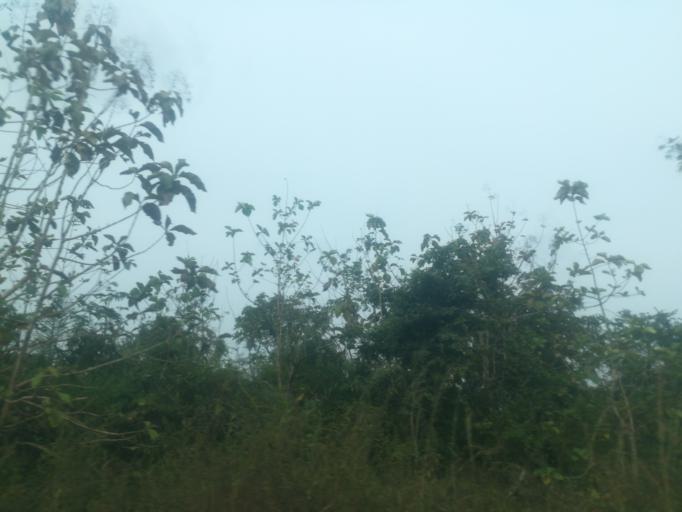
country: NG
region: Ogun
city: Ayetoro
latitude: 7.2801
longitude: 3.0926
